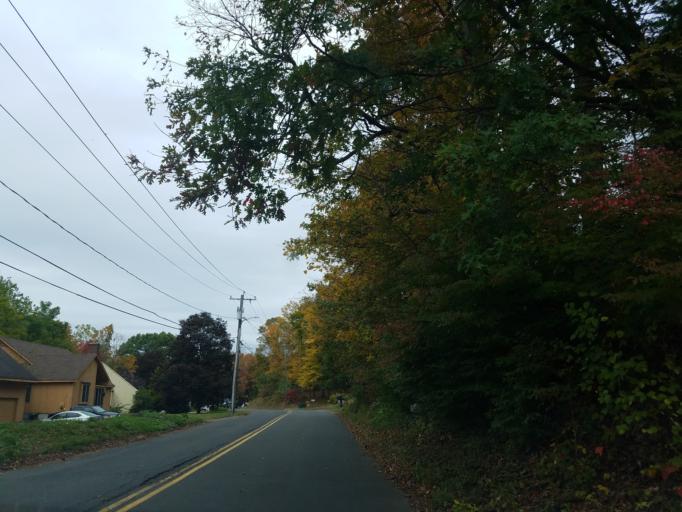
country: US
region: Connecticut
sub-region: New Haven County
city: Cheshire
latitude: 41.4991
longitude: -72.9140
